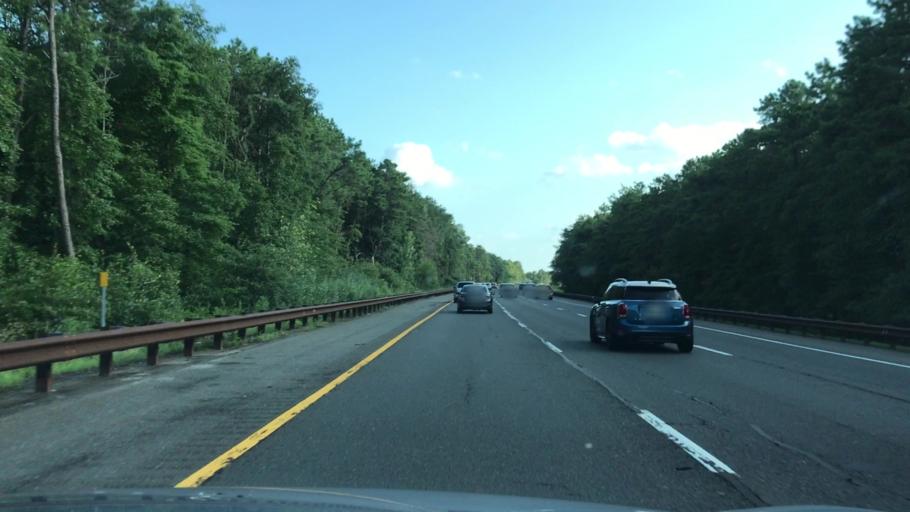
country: US
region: New Jersey
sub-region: Ocean County
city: Forked River
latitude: 39.8382
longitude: -74.2247
